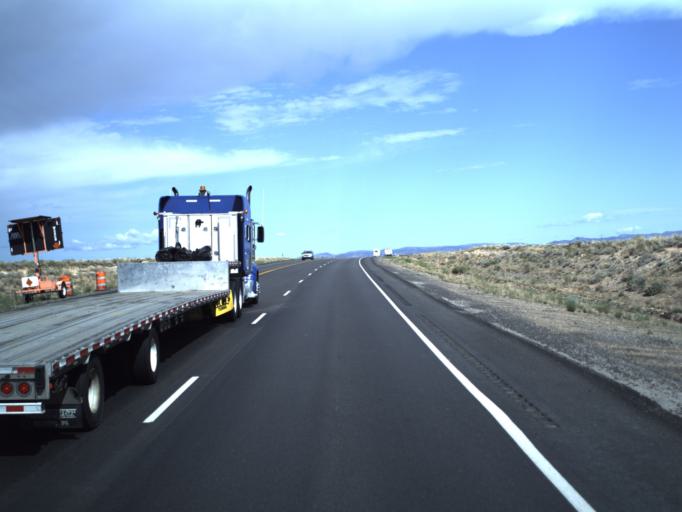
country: US
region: Utah
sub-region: Carbon County
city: East Carbon City
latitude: 39.4781
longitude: -110.5071
